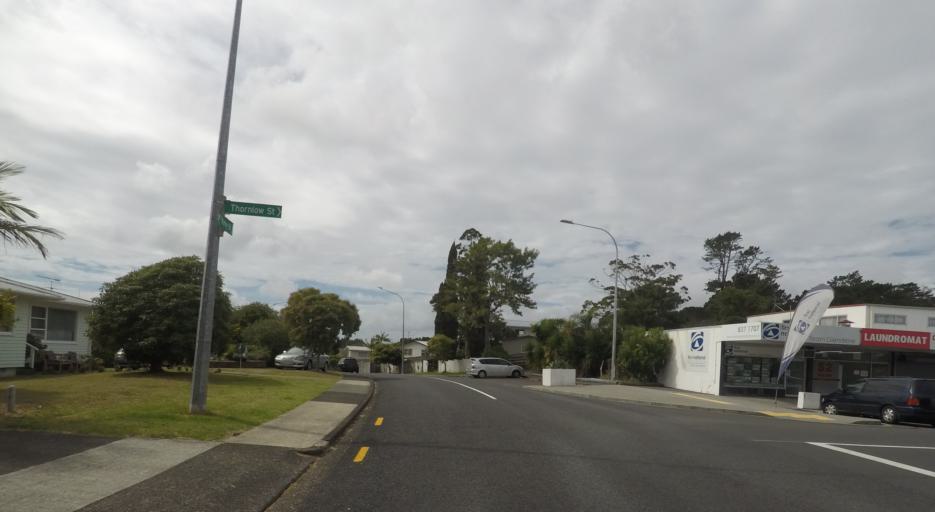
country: NZ
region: Auckland
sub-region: Auckland
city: Rosebank
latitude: -36.8893
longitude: 174.6491
